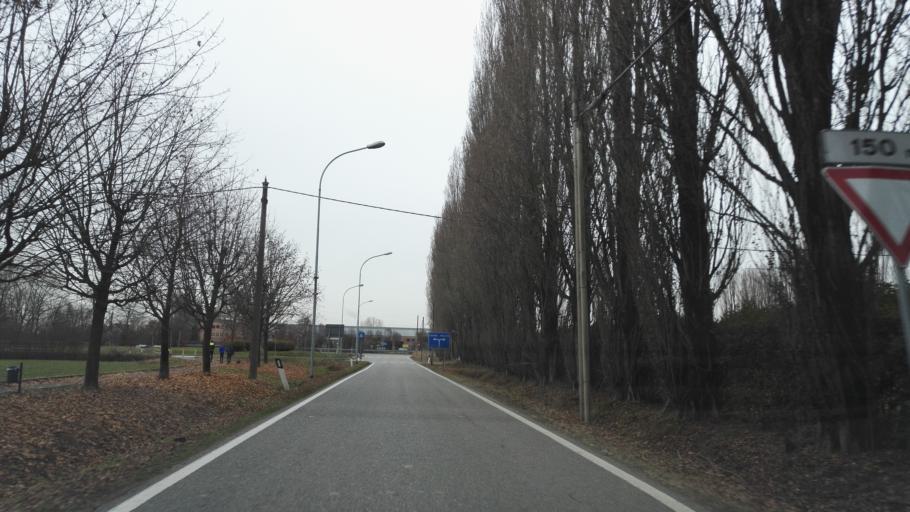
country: IT
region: Lombardy
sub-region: Citta metropolitana di Milano
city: Bettola-Zeloforomagno
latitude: 45.4350
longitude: 9.3243
